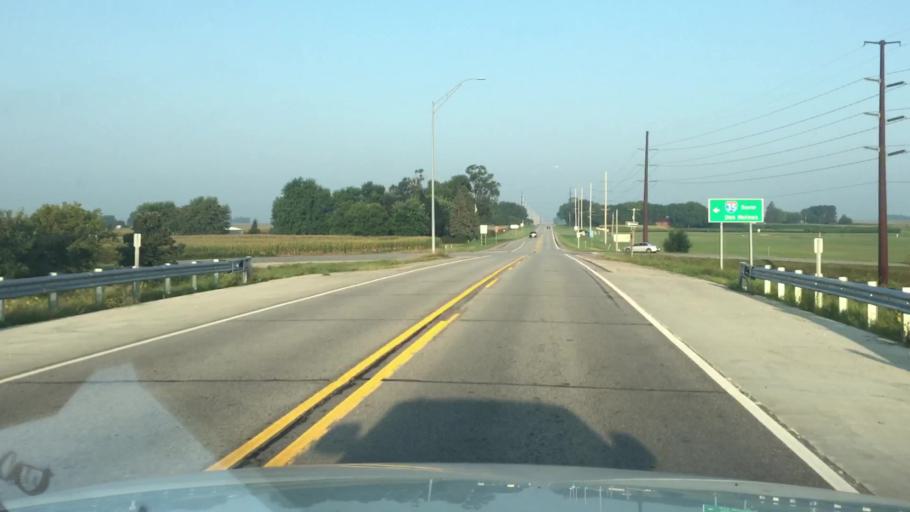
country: US
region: Iowa
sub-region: Story County
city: Huxley
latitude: 41.8778
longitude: -93.5720
